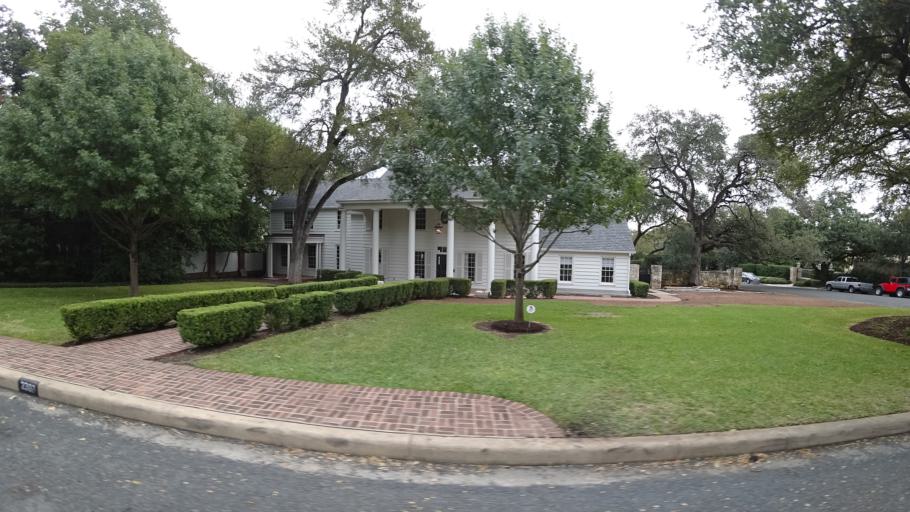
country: US
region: Texas
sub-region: Travis County
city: Austin
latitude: 30.2901
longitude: -97.7581
